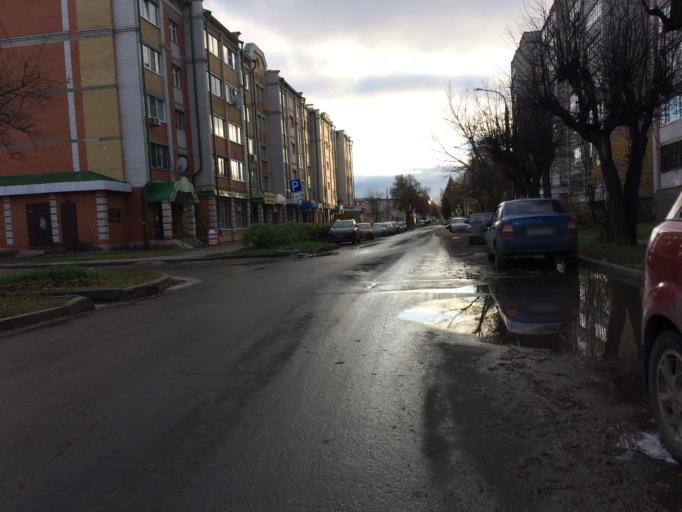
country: RU
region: Mariy-El
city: Yoshkar-Ola
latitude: 56.6432
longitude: 47.9006
